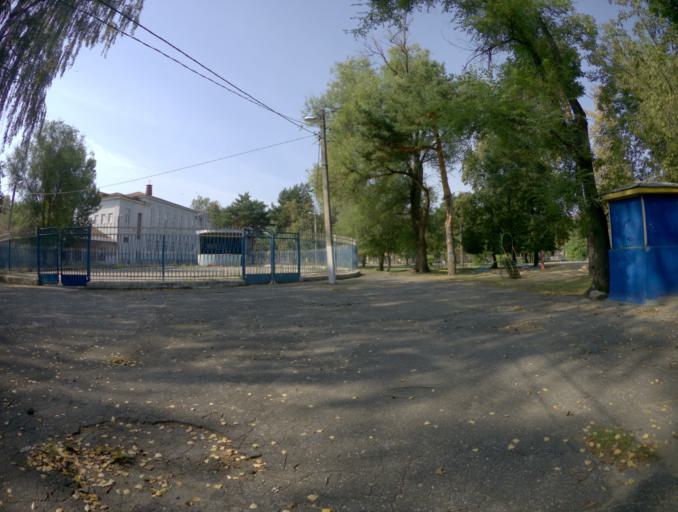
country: RU
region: Vladimir
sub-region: Kovrovskiy Rayon
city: Kovrov
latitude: 56.3727
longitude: 41.3076
